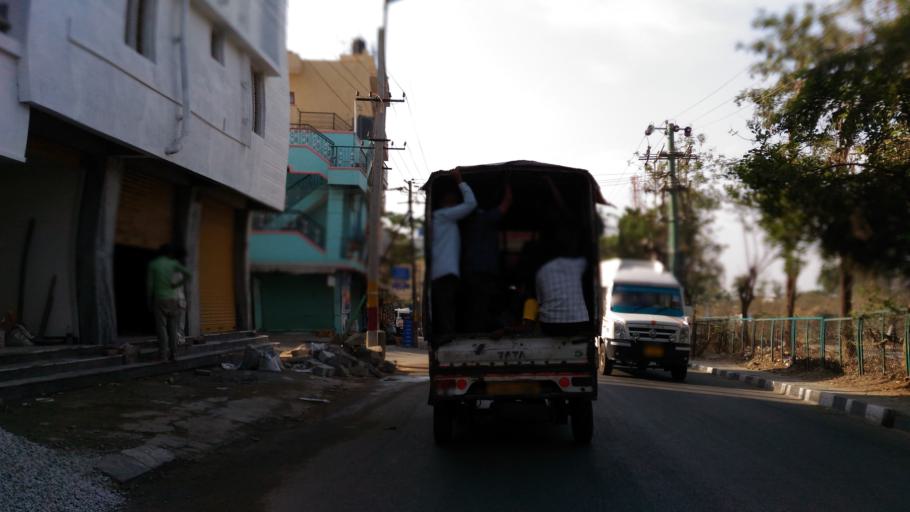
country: IN
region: Karnataka
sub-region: Bangalore Urban
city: Bangalore
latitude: 12.9401
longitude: 77.5340
